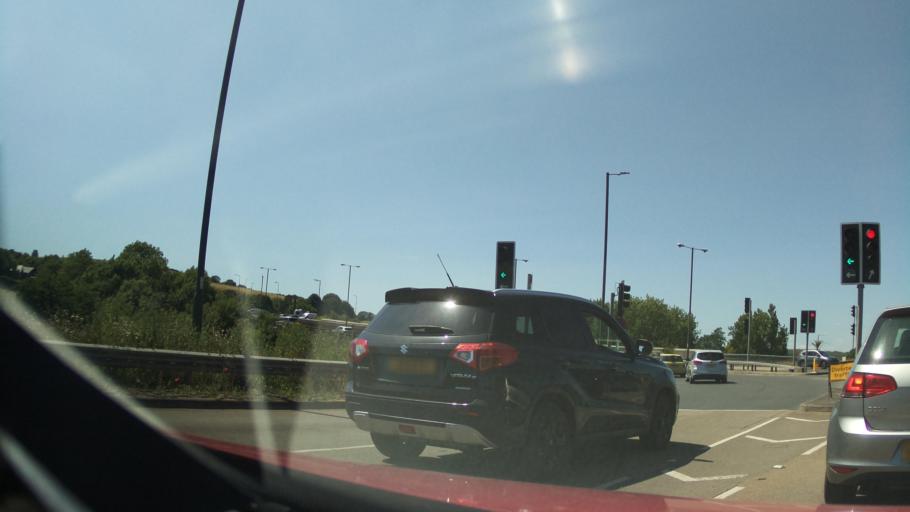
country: GB
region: England
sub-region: Devon
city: Kingskerswell
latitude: 50.4870
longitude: -3.5678
